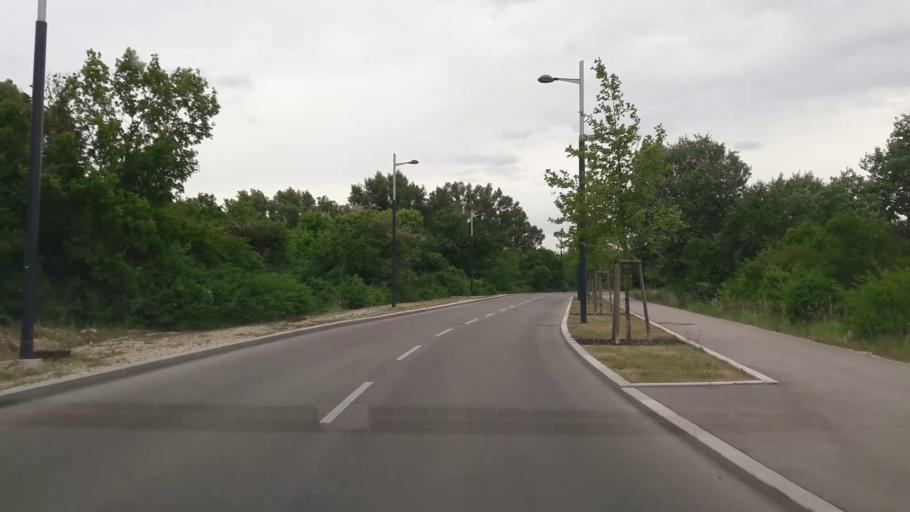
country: AT
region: Lower Austria
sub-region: Politischer Bezirk Ganserndorf
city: Gross-Enzersdorf
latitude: 48.2164
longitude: 16.5103
